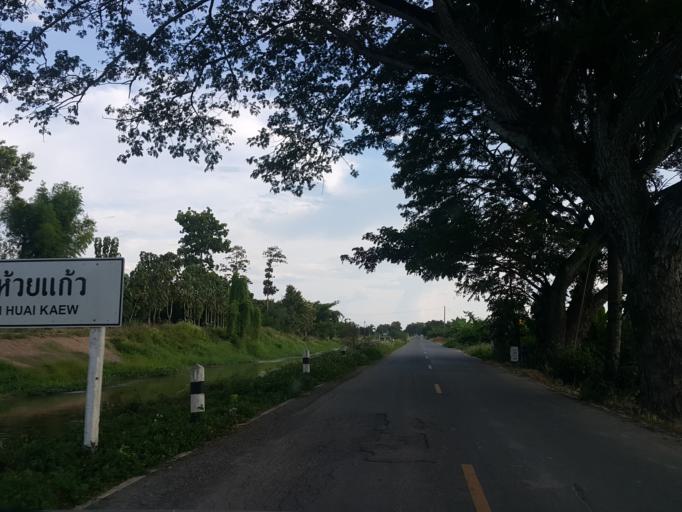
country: TH
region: Chiang Mai
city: Mae Taeng
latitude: 19.0540
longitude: 98.9741
